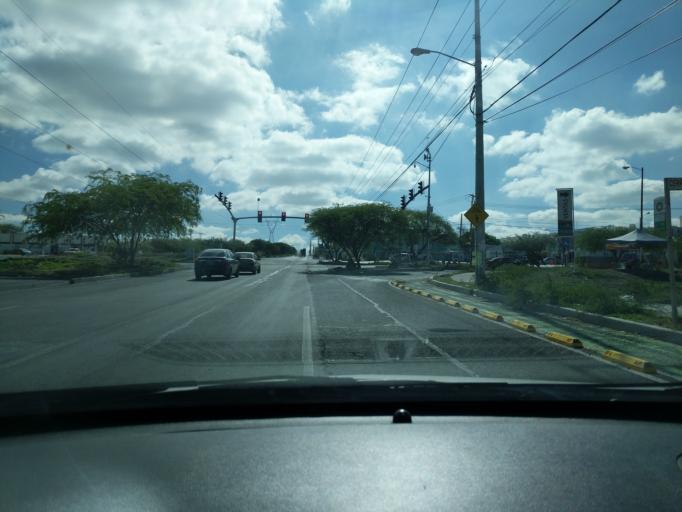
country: MX
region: Queretaro
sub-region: Queretaro
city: Patria Nueva
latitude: 20.6417
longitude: -100.4923
